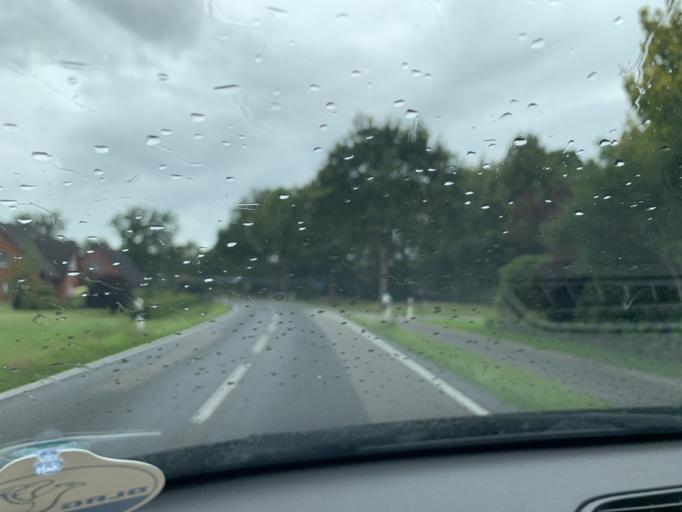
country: DE
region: Lower Saxony
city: Apen
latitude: 53.1622
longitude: 7.8582
